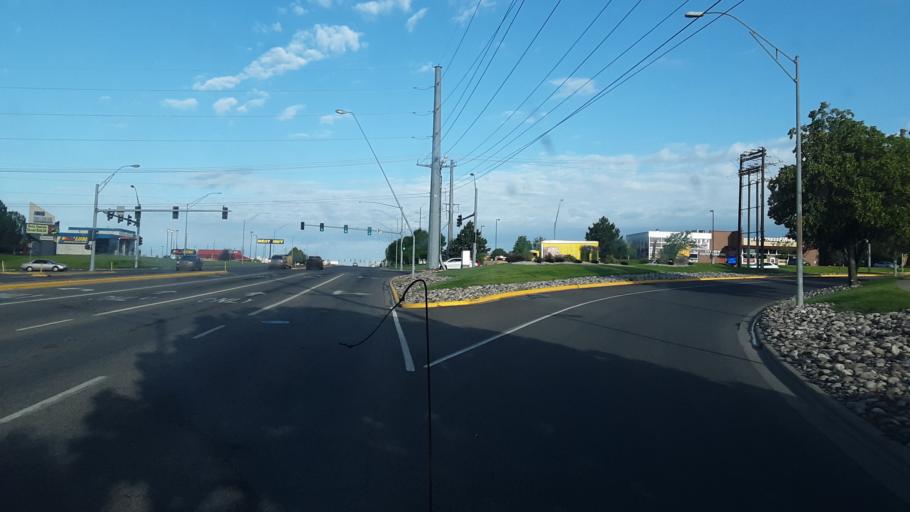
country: US
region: Montana
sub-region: Yellowstone County
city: Billings
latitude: 45.7552
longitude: -108.5749
